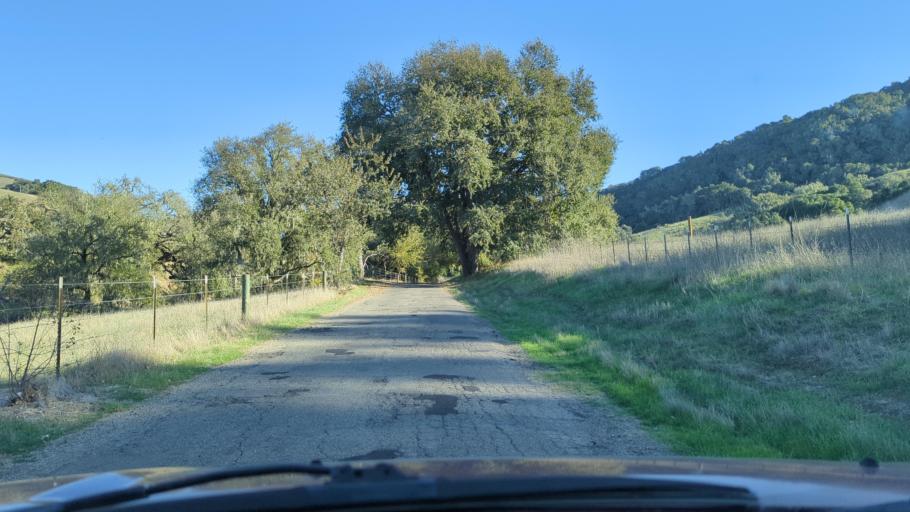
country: US
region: California
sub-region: Santa Barbara County
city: Santa Ynez
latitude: 34.5652
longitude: -120.0934
